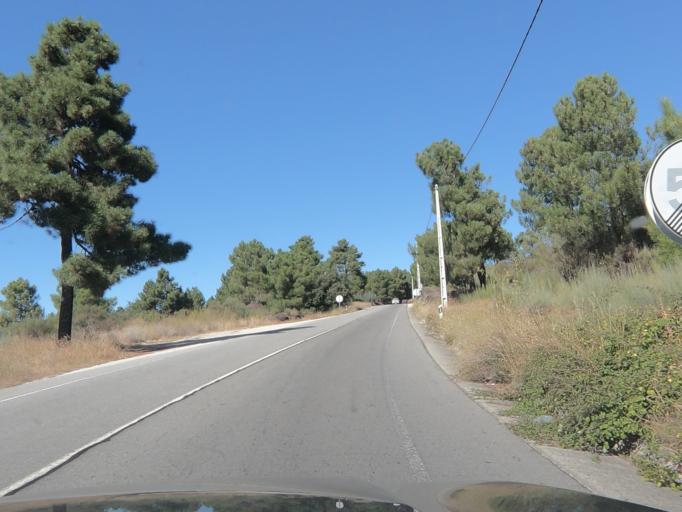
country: PT
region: Vila Real
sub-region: Valpacos
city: Valpacos
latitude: 41.6326
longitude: -7.3179
